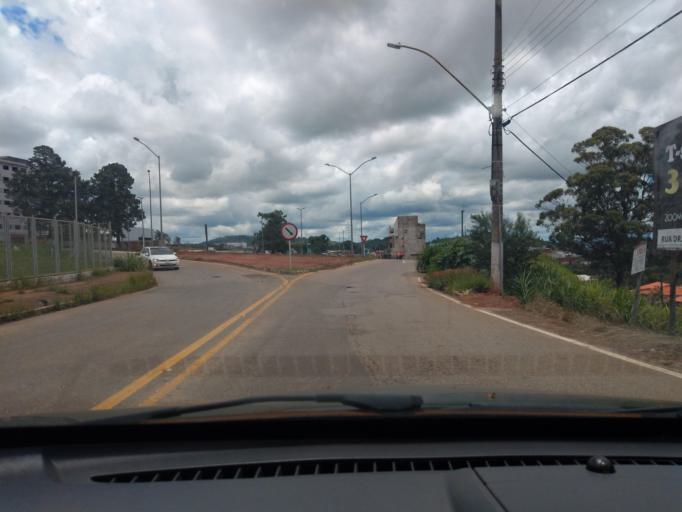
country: BR
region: Minas Gerais
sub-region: Lavras
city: Lavras
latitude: -21.2388
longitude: -45.0244
